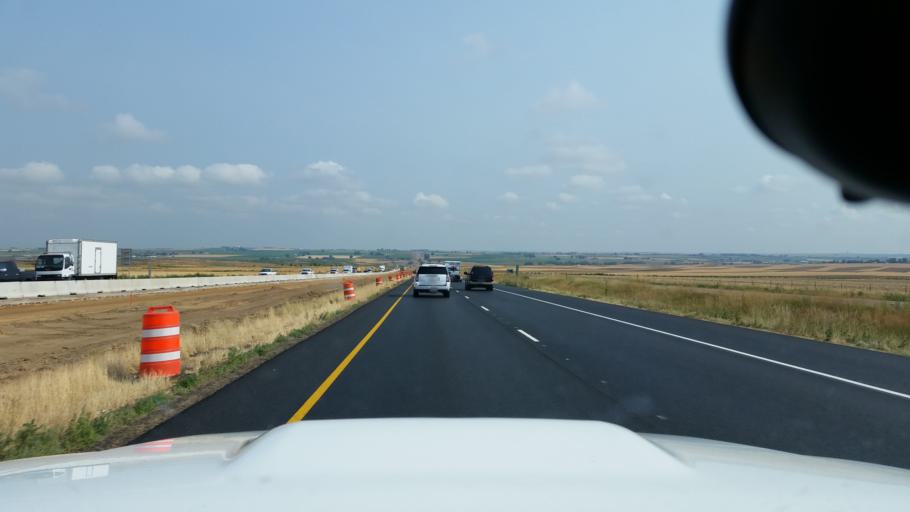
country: US
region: Colorado
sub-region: Weld County
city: Mead
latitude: 40.2731
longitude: -104.9801
